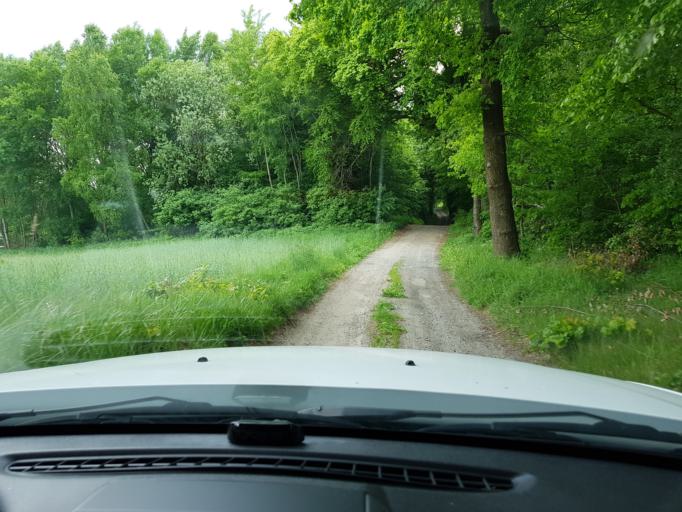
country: PL
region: West Pomeranian Voivodeship
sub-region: Powiat drawski
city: Drawsko Pomorskie
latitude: 53.5456
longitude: 15.7373
